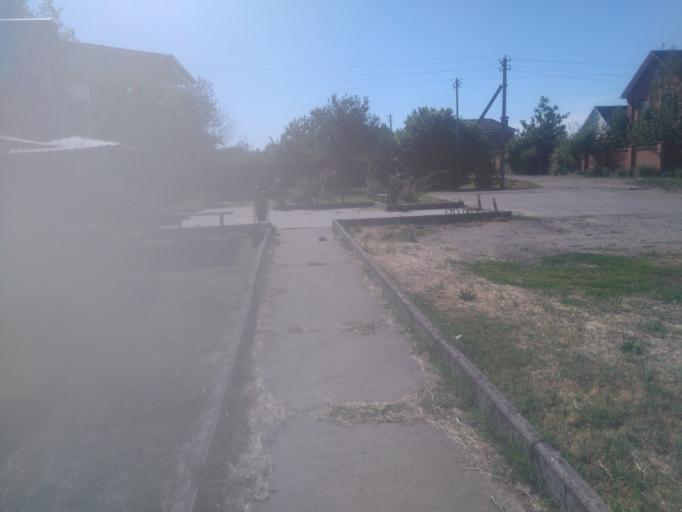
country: RU
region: Krasnodarskiy
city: Fastovetskaya
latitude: 45.9068
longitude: 40.1504
